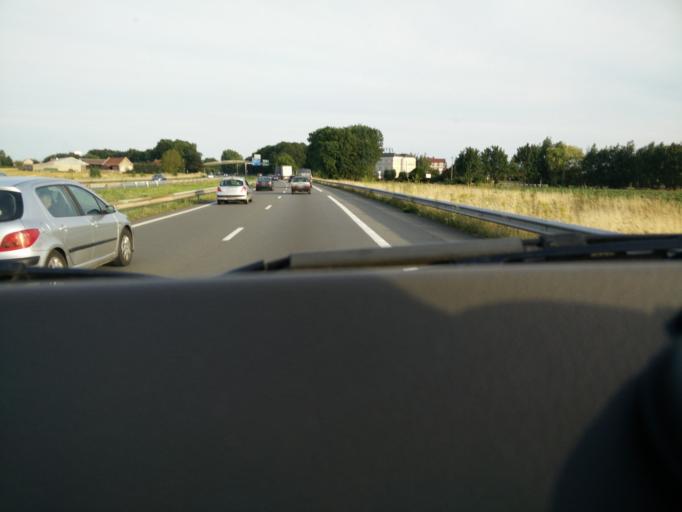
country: FR
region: Nord-Pas-de-Calais
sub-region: Departement du Nord
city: Orchies
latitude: 50.4761
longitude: 3.2209
